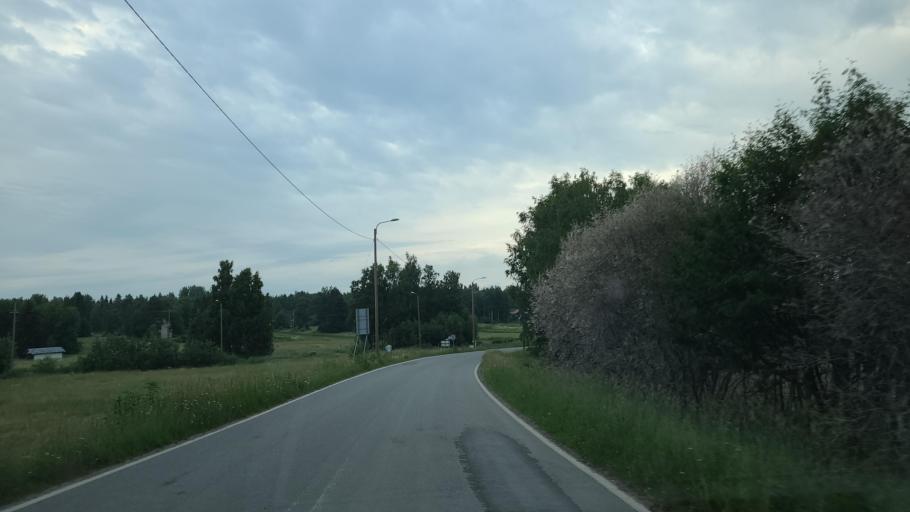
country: FI
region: Ostrobothnia
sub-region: Vaasa
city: Replot
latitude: 63.1818
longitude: 21.2810
